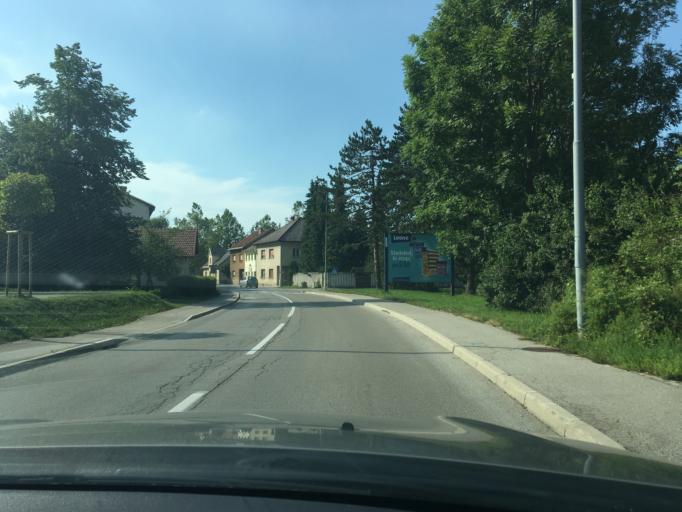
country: SI
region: Ribnica
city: Ribnica
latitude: 45.7368
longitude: 14.7300
